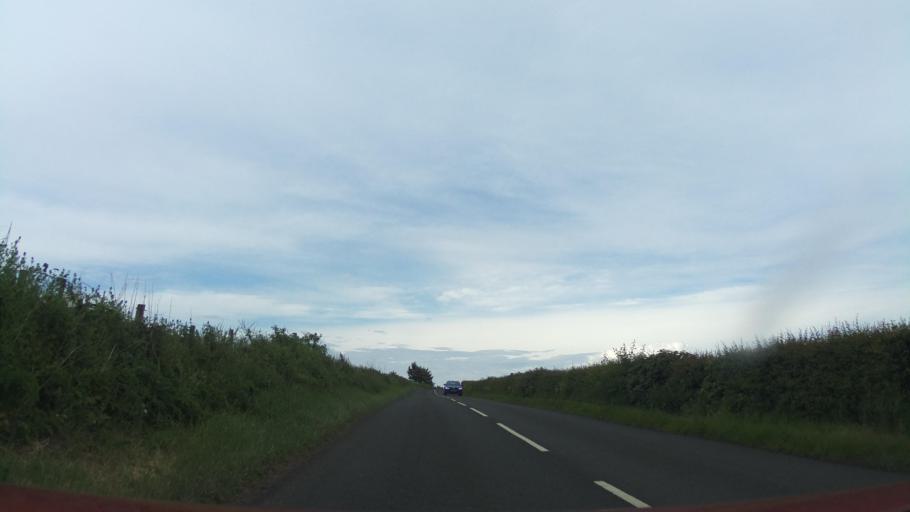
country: GB
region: Scotland
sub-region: East Lothian
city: Prestonpans
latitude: 55.9146
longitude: -3.0009
